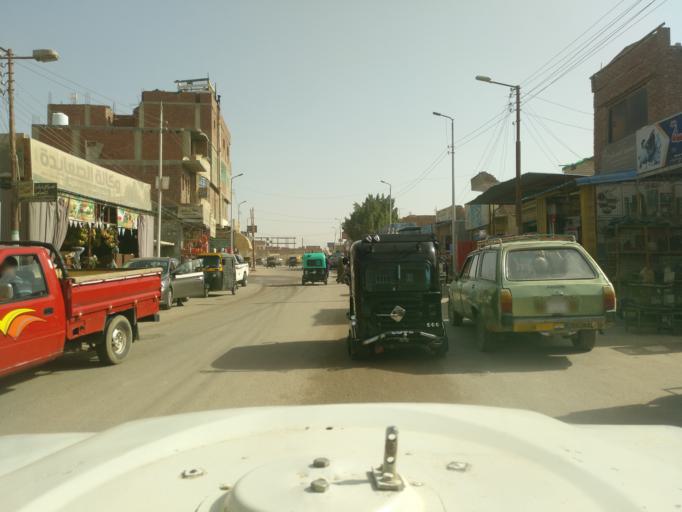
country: EG
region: Al Buhayrah
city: Beheira
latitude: 30.3773
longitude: 30.3483
